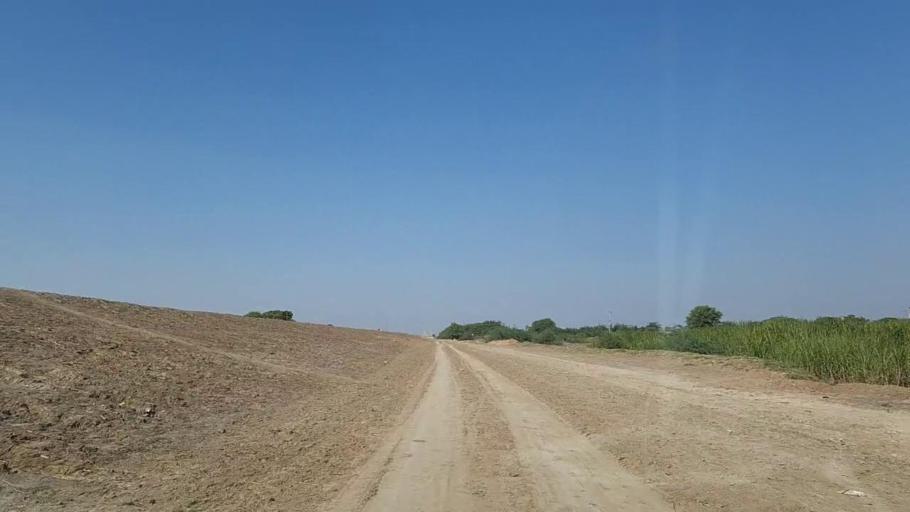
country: PK
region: Sindh
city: Chuhar Jamali
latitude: 24.5359
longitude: 68.0159
